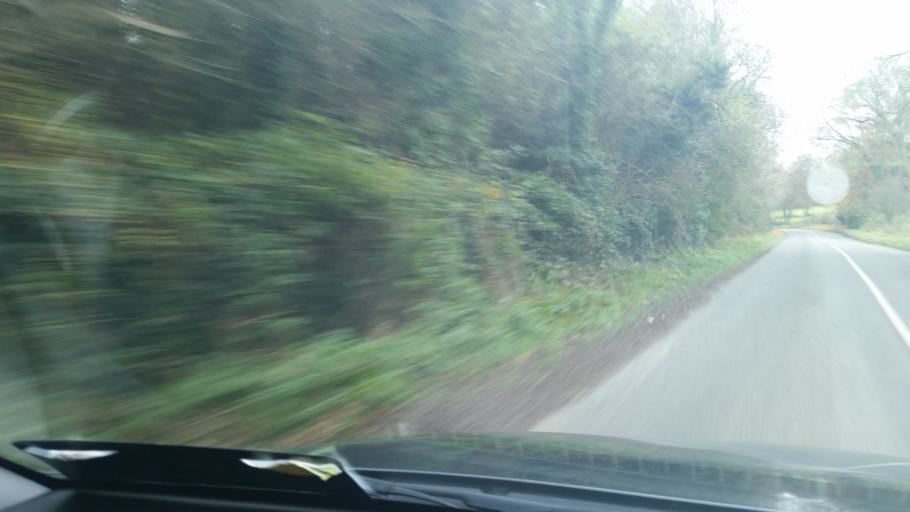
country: IE
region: Leinster
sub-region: An Mhi
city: Duleek
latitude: 53.6947
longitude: -6.4300
